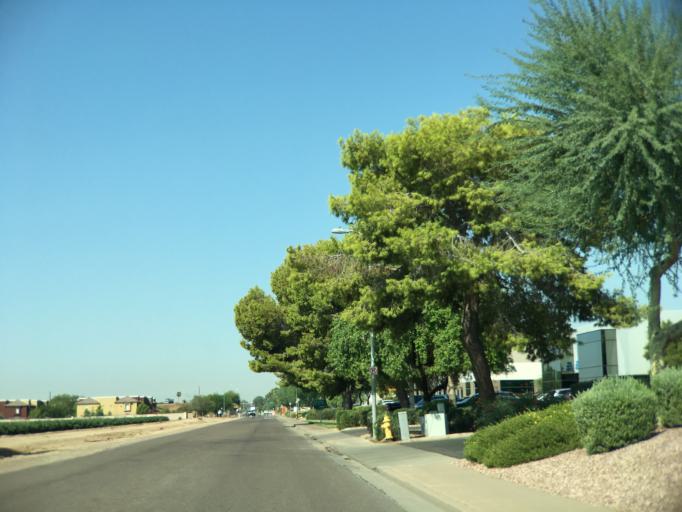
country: US
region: Arizona
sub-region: Maricopa County
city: Glendale
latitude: 33.4588
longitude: -112.1787
